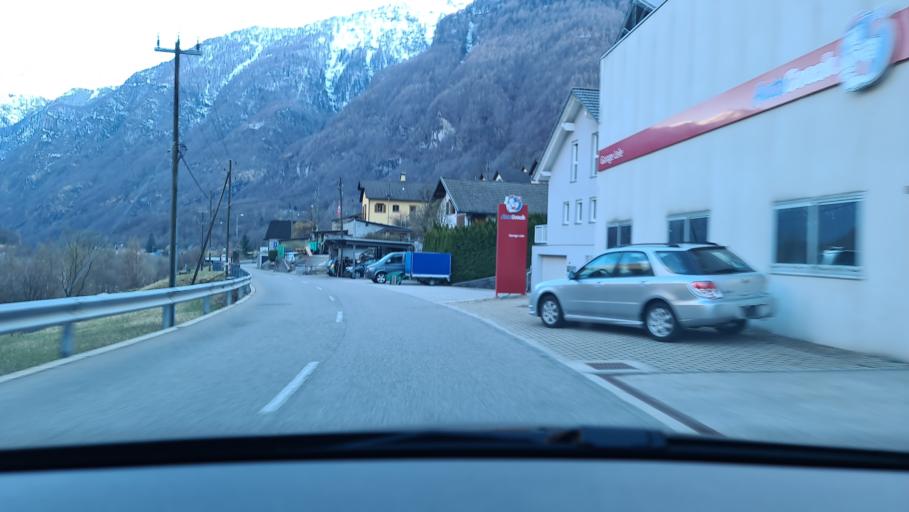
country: CH
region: Ticino
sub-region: Locarno District
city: Lavertezzo
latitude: 46.3004
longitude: 8.7926
